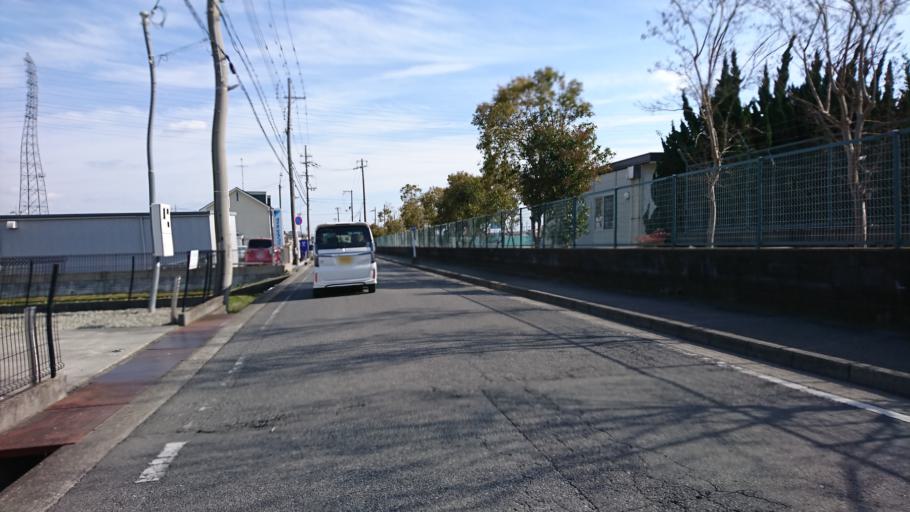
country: JP
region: Hyogo
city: Kakogawacho-honmachi
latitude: 34.7877
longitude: 134.8280
